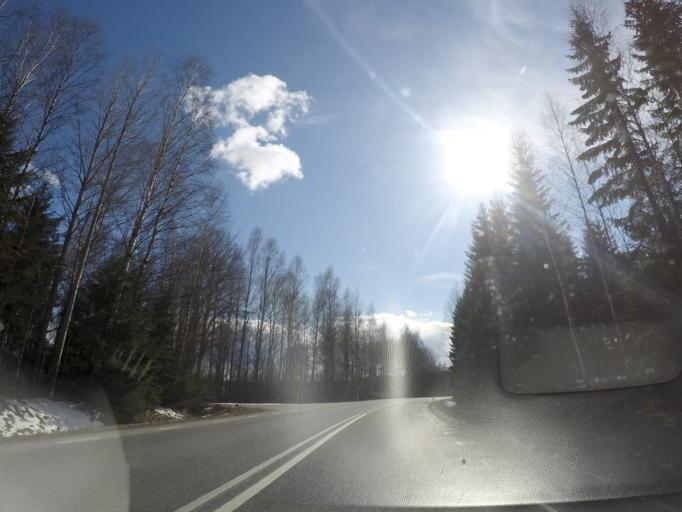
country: SE
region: Vaestmanland
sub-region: Skinnskattebergs Kommun
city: Skinnskatteberg
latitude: 59.8383
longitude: 15.6824
